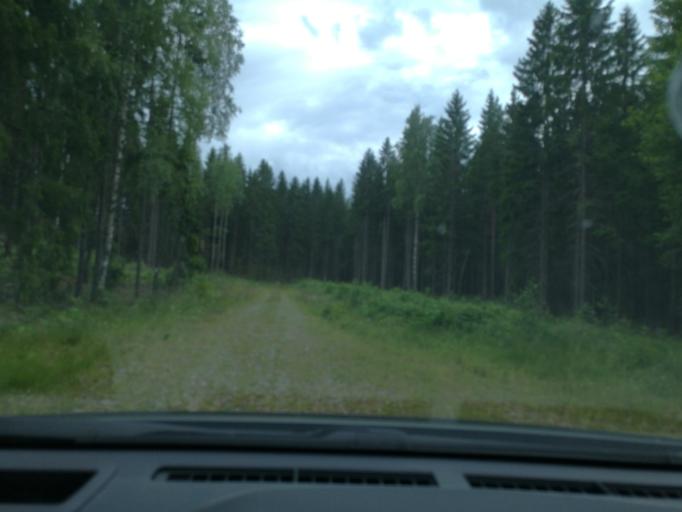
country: SE
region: Vaestmanland
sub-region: Surahammars Kommun
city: Ramnas
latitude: 59.8036
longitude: 16.3204
